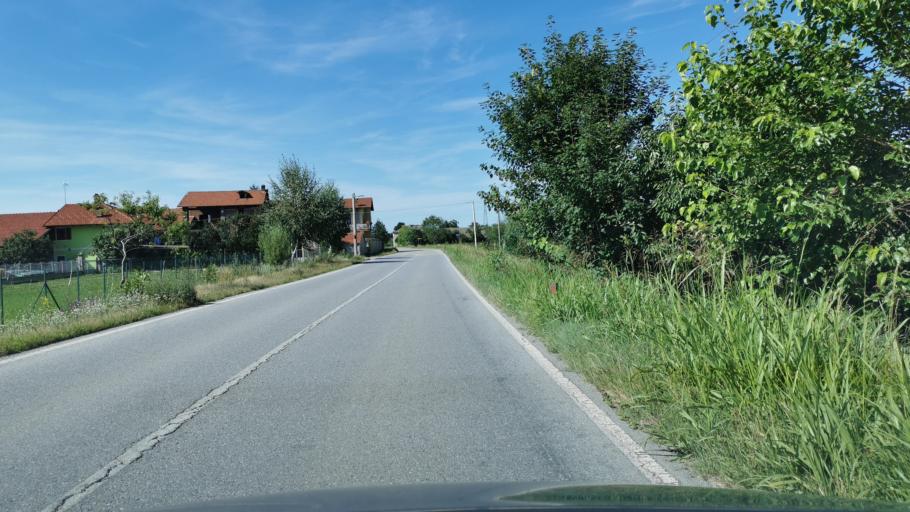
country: IT
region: Piedmont
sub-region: Provincia di Cuneo
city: Boves
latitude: 44.3471
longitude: 7.5581
